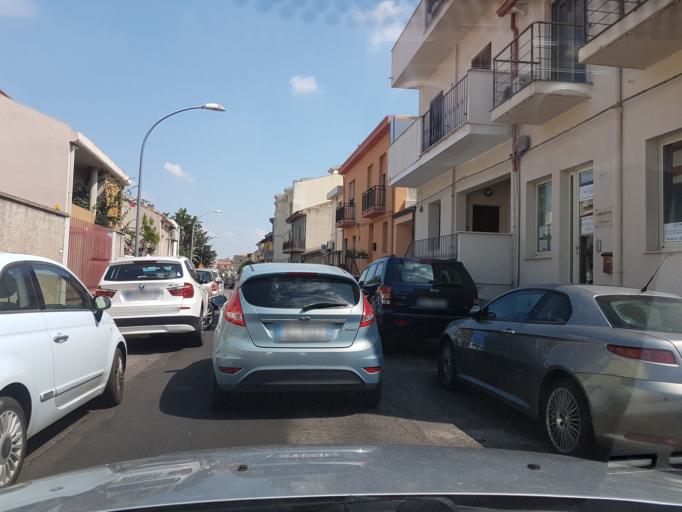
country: IT
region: Sardinia
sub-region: Provincia di Oristano
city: Oristano
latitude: 39.9044
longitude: 8.5991
